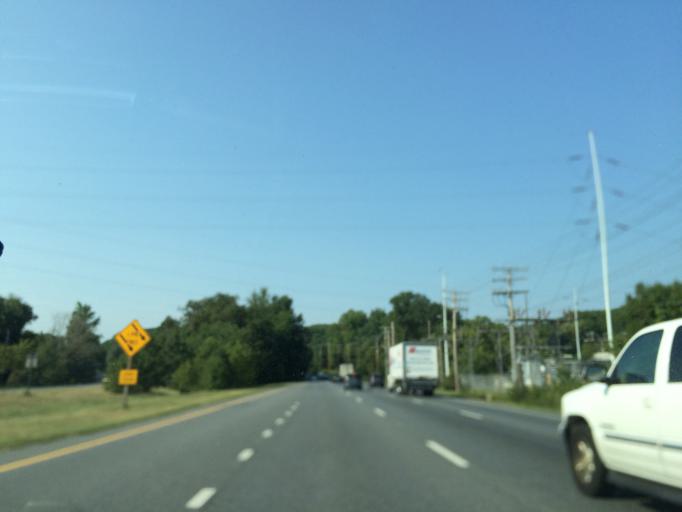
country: US
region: Maryland
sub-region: Anne Arundel County
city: Crofton
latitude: 38.9843
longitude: -76.7104
